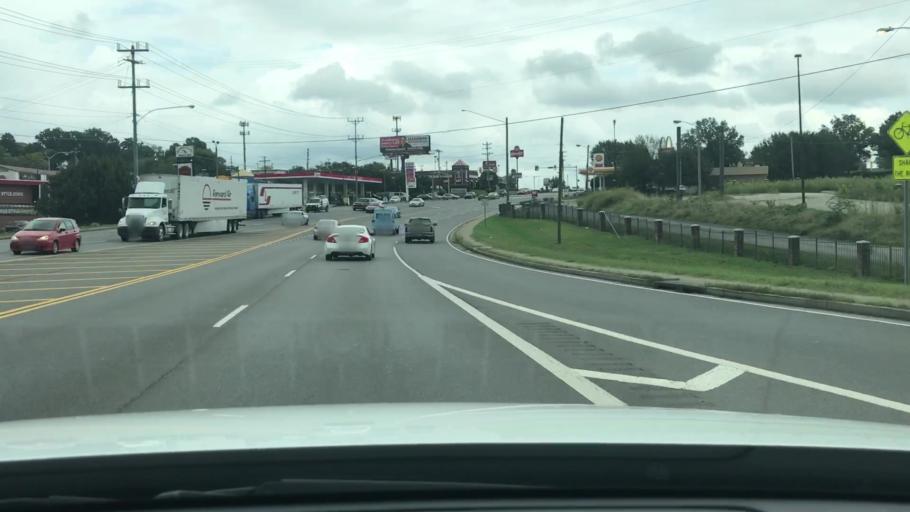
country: US
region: Tennessee
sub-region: Davidson County
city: Oak Hill
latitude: 36.0865
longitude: -86.6983
